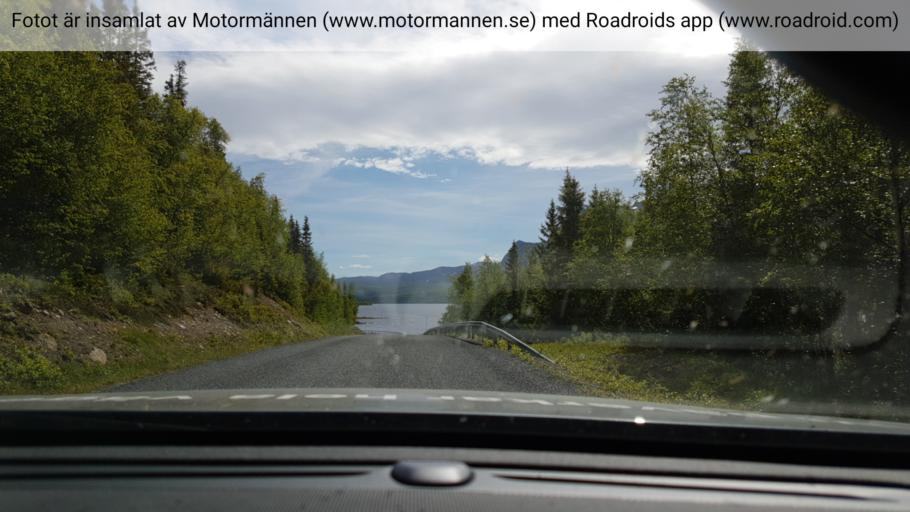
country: SE
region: Vaesterbotten
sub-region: Vilhelmina Kommun
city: Sjoberg
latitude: 65.2608
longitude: 15.3846
